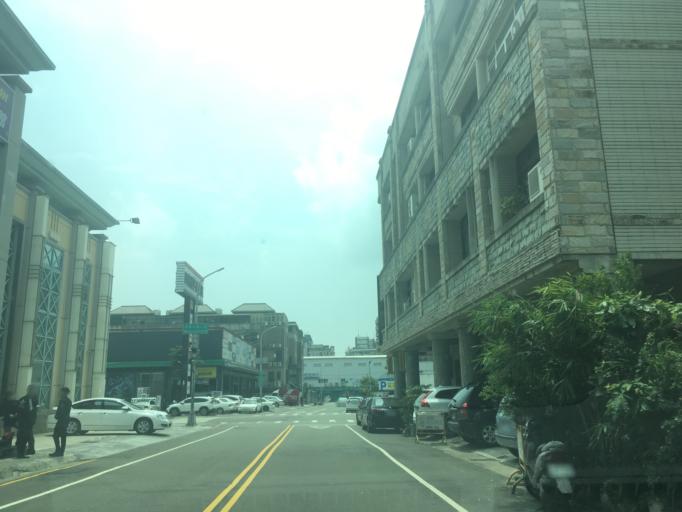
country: TW
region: Taiwan
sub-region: Taichung City
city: Taichung
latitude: 24.1783
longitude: 120.6825
